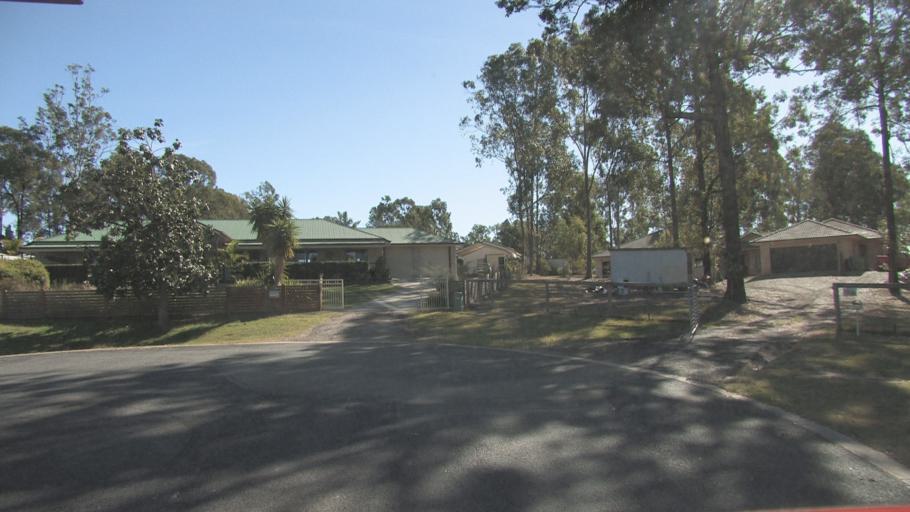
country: AU
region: Queensland
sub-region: Logan
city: North Maclean
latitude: -27.7325
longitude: 152.9629
